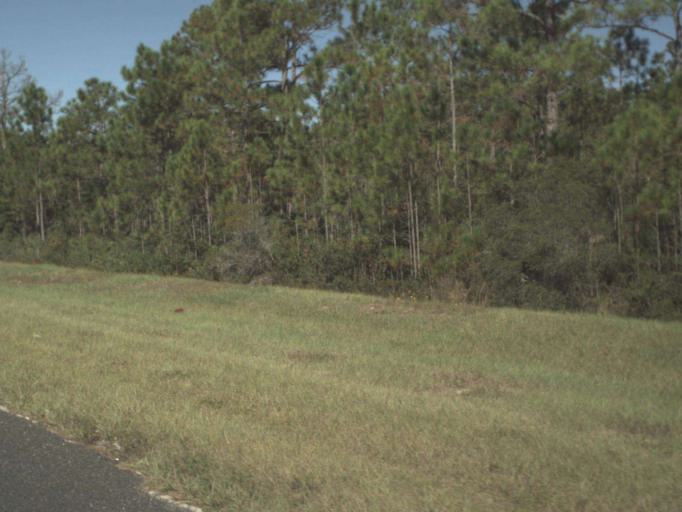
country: US
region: Florida
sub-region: Walton County
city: Miramar Beach
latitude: 30.3756
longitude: -86.2809
